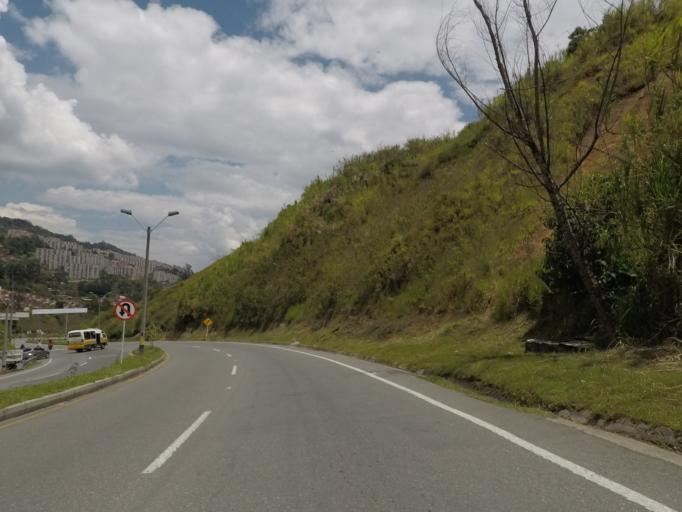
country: CO
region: Antioquia
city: Medellin
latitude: 6.2751
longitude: -75.6293
